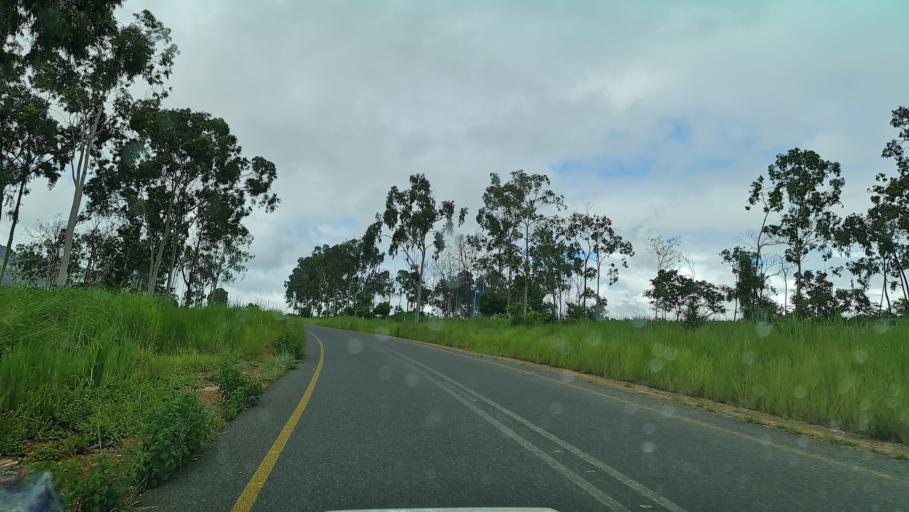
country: MZ
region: Nampula
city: Nampula
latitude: -14.9845
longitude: 38.5178
